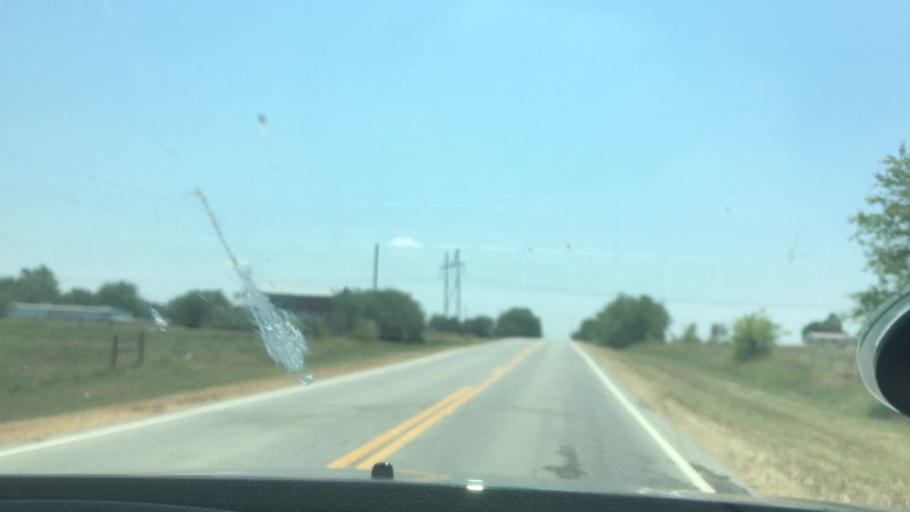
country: US
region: Oklahoma
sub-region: Coal County
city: Coalgate
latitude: 34.5228
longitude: -96.4070
